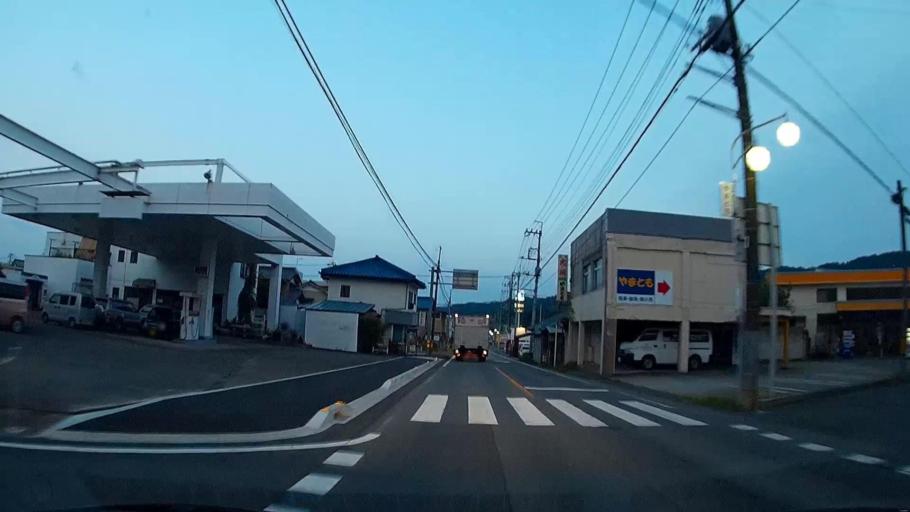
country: JP
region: Gunma
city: Annaka
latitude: 36.3833
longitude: 138.8821
